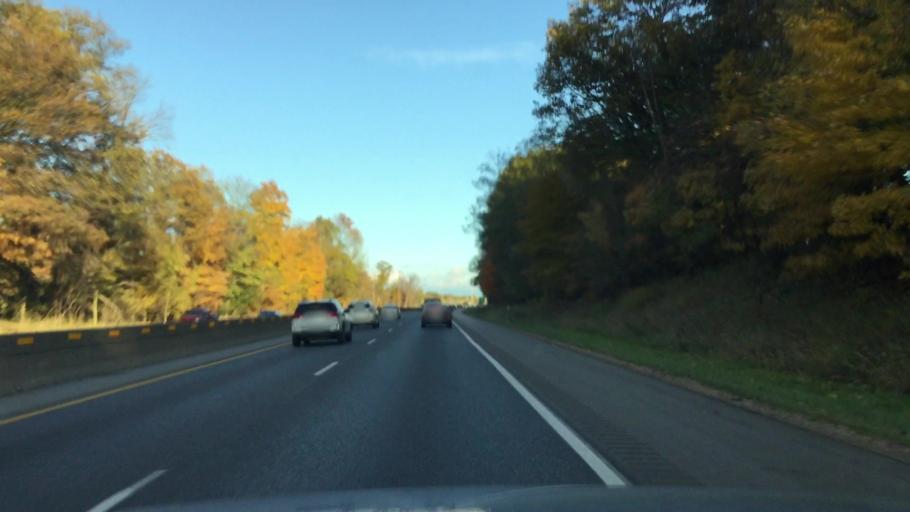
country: US
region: Michigan
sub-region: Kalamazoo County
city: Galesburg
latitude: 42.2801
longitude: -85.3890
